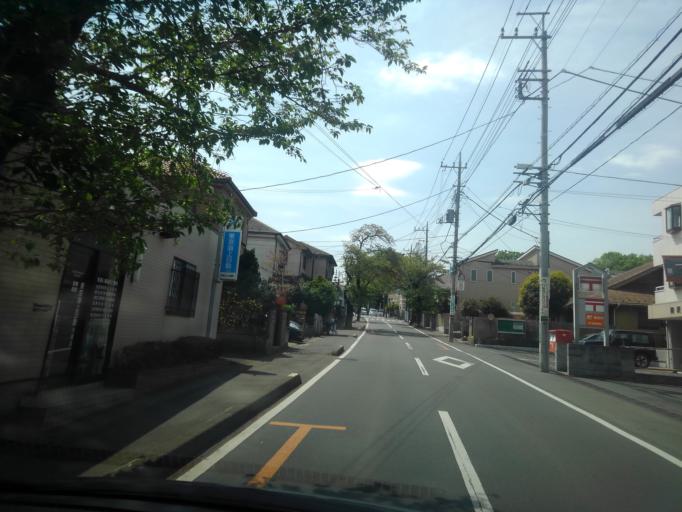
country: JP
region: Saitama
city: Tokorozawa
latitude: 35.7863
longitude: 139.4393
